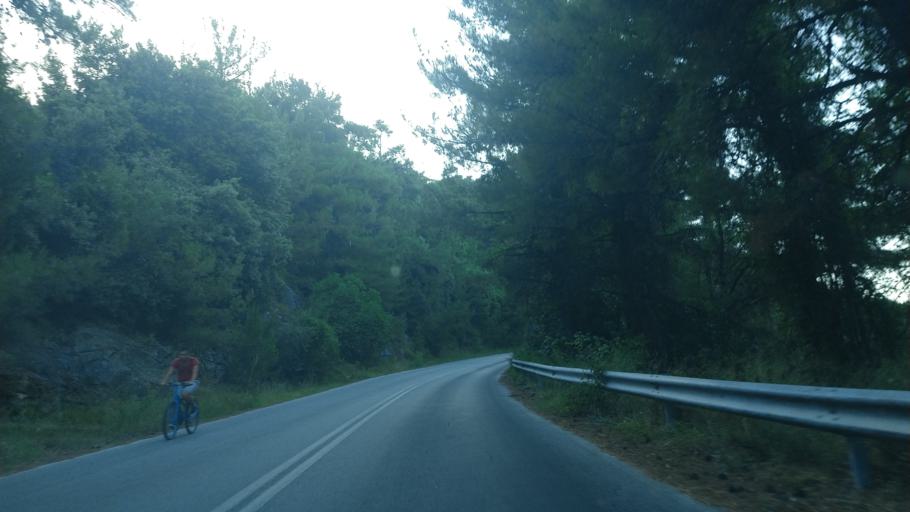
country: GR
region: East Macedonia and Thrace
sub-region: Nomos Kavalas
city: Potamia
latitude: 40.7217
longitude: 24.7347
